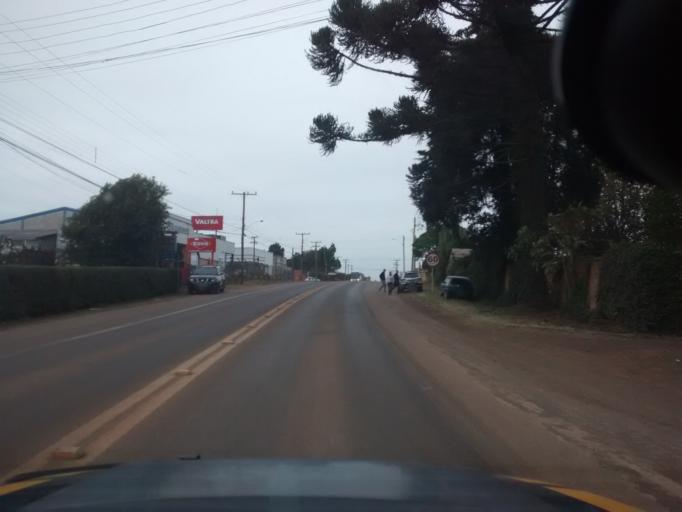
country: BR
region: Rio Grande do Sul
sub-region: Vacaria
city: Vacaria
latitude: -28.4915
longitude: -50.9559
